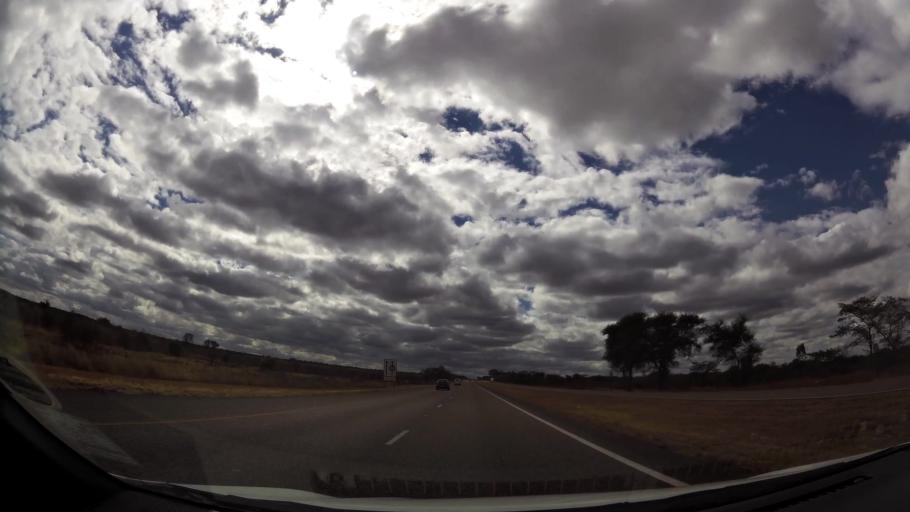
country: ZA
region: Limpopo
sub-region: Waterberg District Municipality
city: Bela-Bela
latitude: -24.8844
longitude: 28.3847
